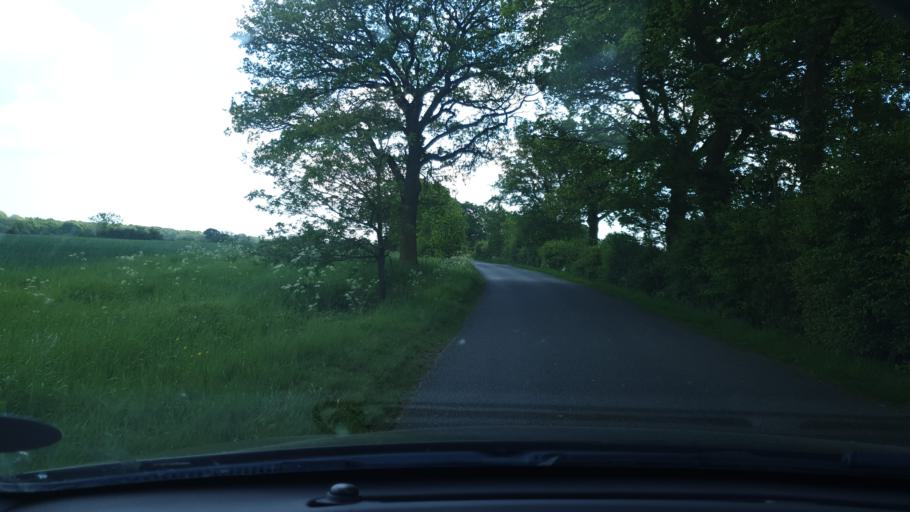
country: GB
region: England
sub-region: Essex
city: Great Bentley
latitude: 51.8477
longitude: 1.0889
